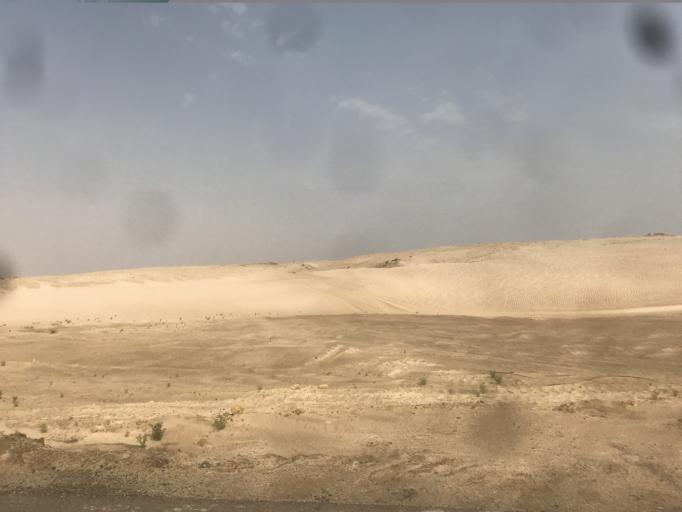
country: SA
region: Eastern Province
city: Abqaiq
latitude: 25.9061
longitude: 50.0063
